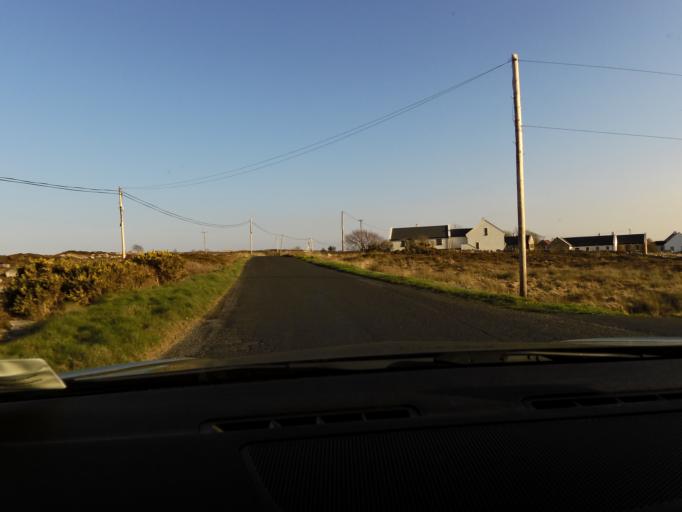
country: IE
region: Connaught
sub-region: County Galway
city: Oughterard
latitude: 53.2603
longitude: -9.5455
